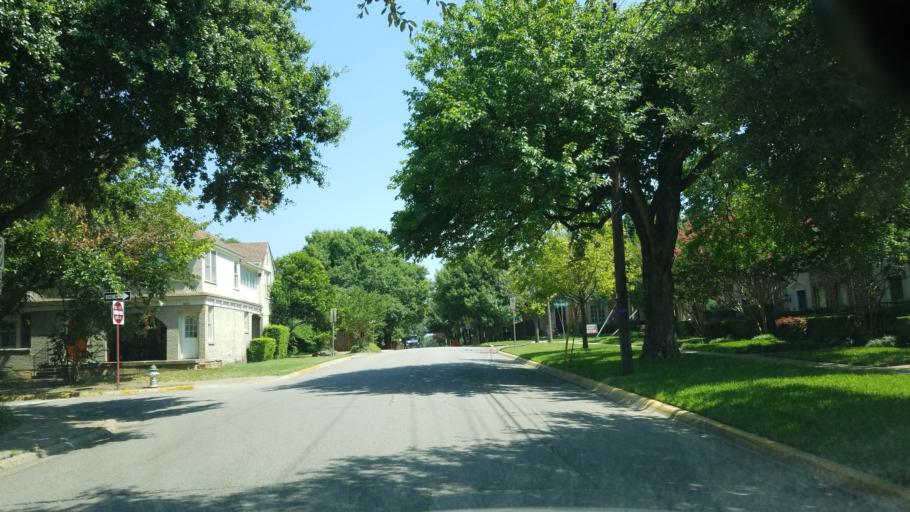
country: US
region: Texas
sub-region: Dallas County
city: Highland Park
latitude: 32.8474
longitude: -96.7829
